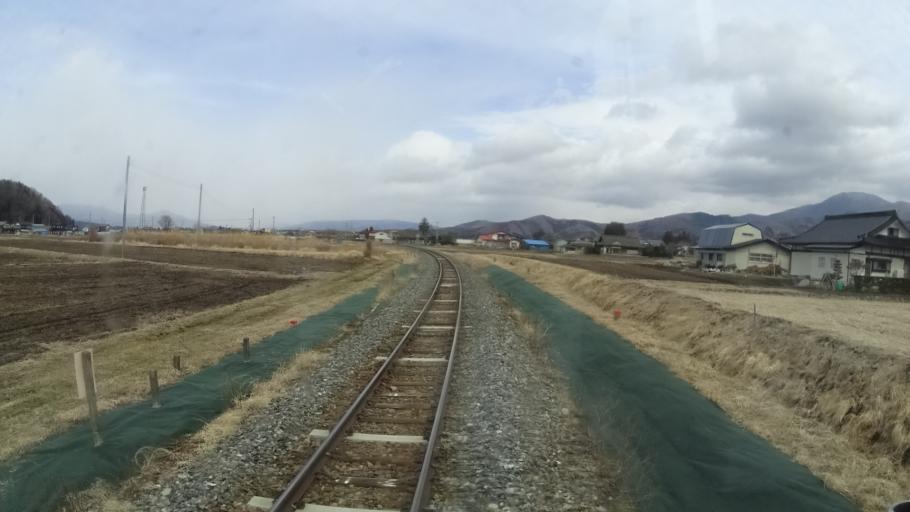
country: JP
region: Iwate
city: Tono
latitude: 39.2776
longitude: 141.5910
